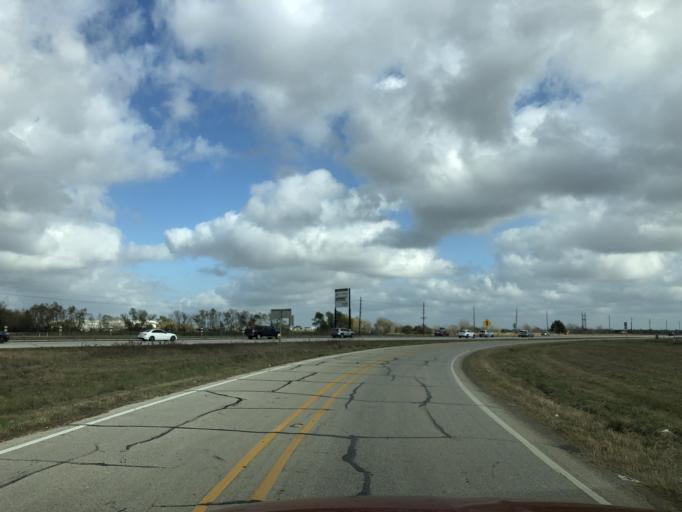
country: US
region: Texas
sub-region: Austin County
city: Sealy
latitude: 29.7584
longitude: -96.2183
